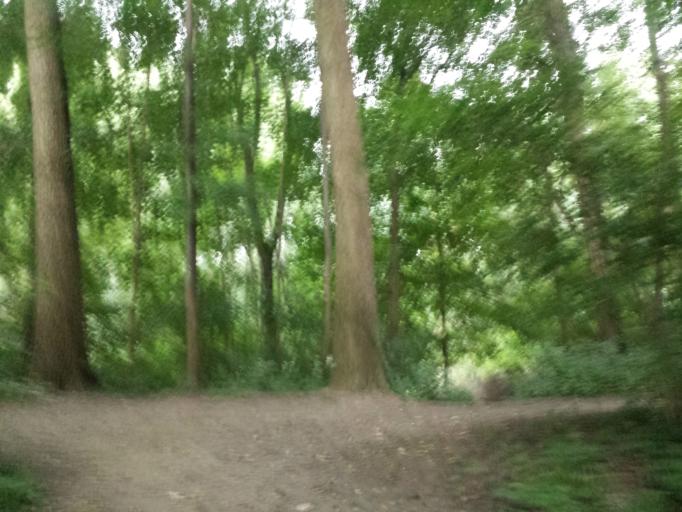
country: DE
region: Rheinland-Pfalz
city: Altrip
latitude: 49.4251
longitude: 8.4978
